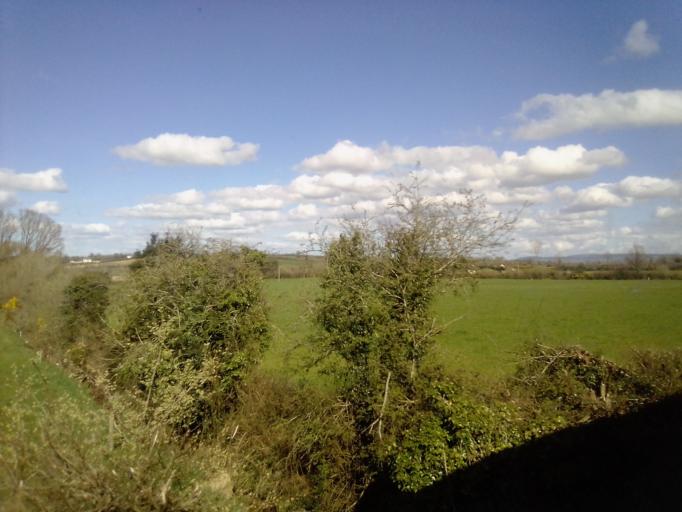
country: IE
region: Munster
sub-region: County Cork
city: Kanturk
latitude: 52.1254
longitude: -8.8183
